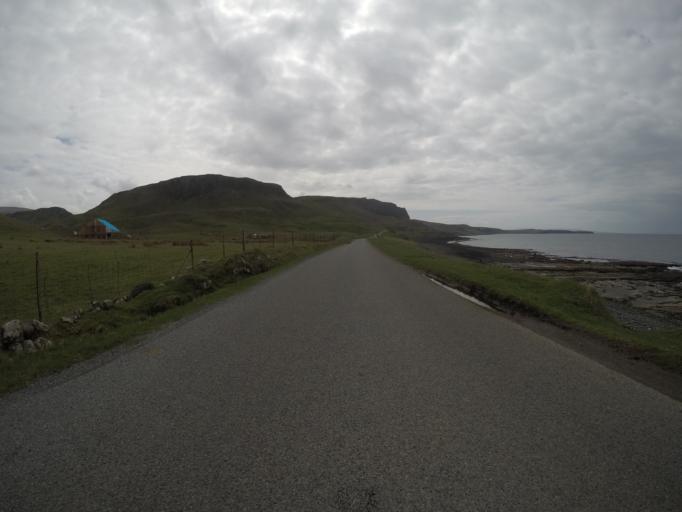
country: GB
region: Scotland
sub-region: Highland
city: Portree
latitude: 57.6802
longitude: -6.3444
